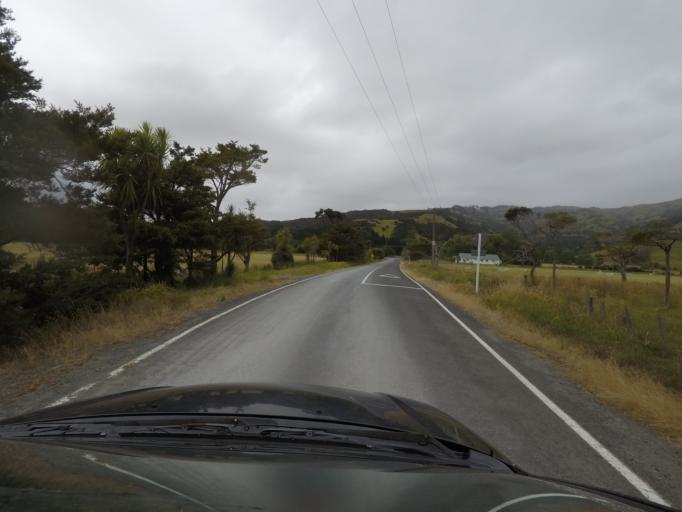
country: NZ
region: Auckland
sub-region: Auckland
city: Warkworth
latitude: -36.2622
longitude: 174.7265
